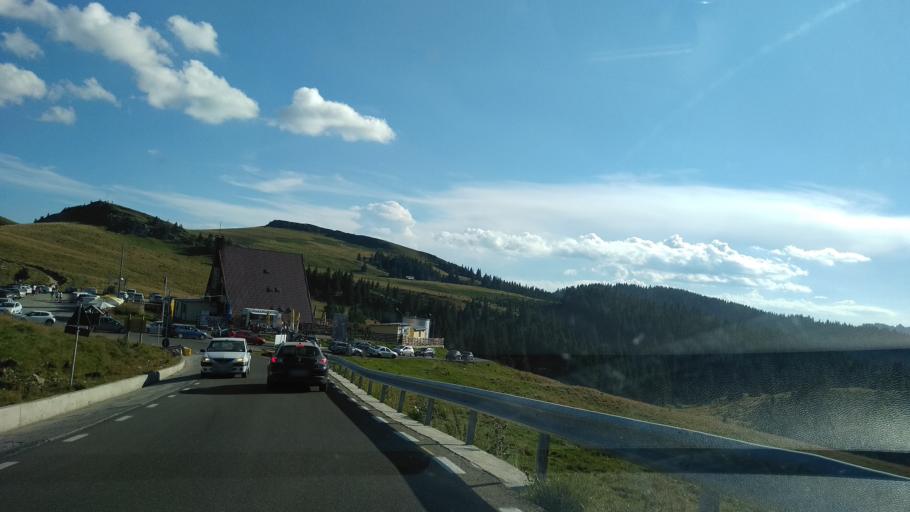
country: RO
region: Dambovita
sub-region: Comuna Moroeni
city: Glod
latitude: 45.3279
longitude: 25.4636
